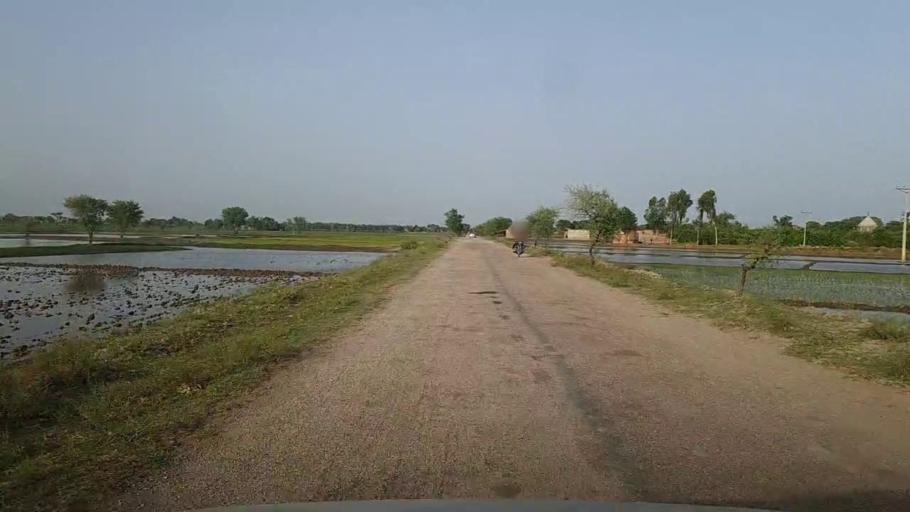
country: PK
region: Sindh
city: Khairpur Nathan Shah
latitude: 27.1584
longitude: 67.7518
